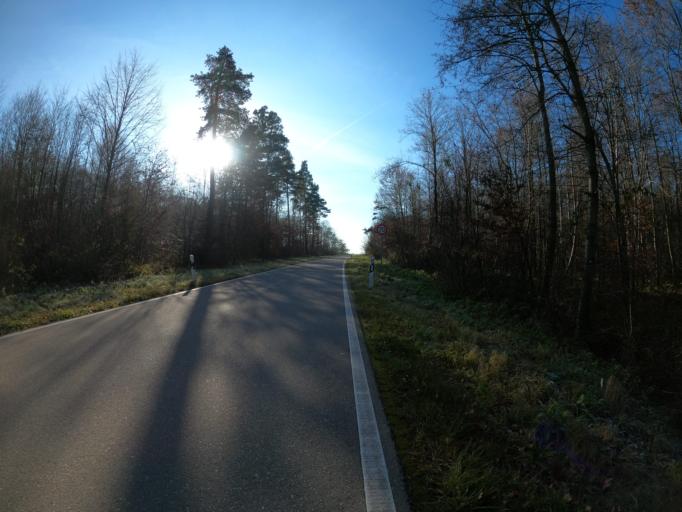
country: DE
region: Baden-Wuerttemberg
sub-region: Regierungsbezirk Stuttgart
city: Schlierbach
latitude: 48.6904
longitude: 9.5355
